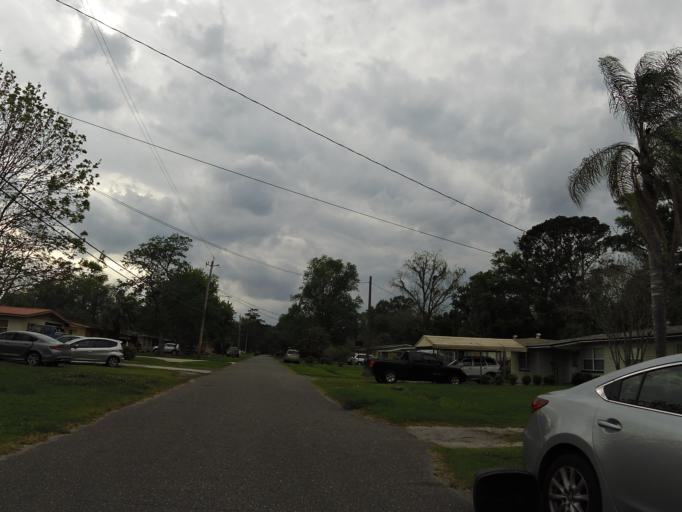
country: US
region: Florida
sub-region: Duval County
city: Jacksonville
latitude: 30.2929
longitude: -81.7349
